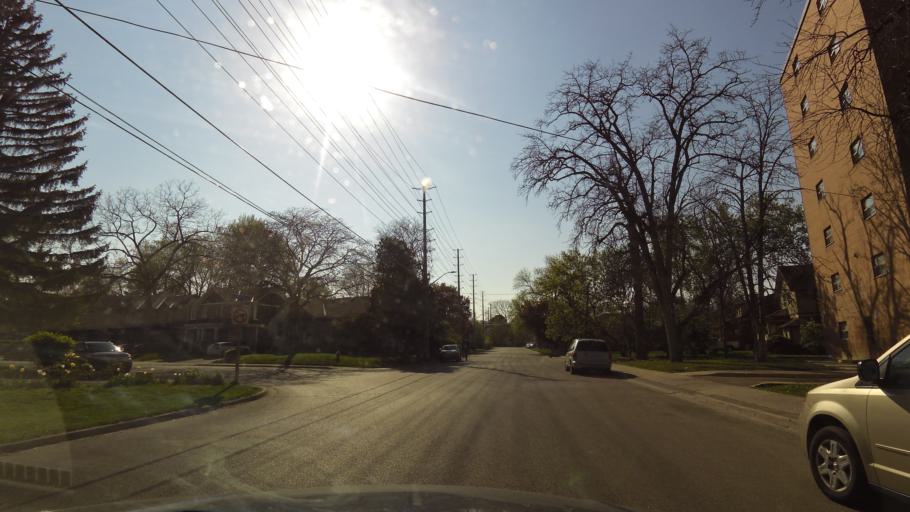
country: CA
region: Ontario
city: Mississauga
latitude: 43.5632
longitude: -79.5758
